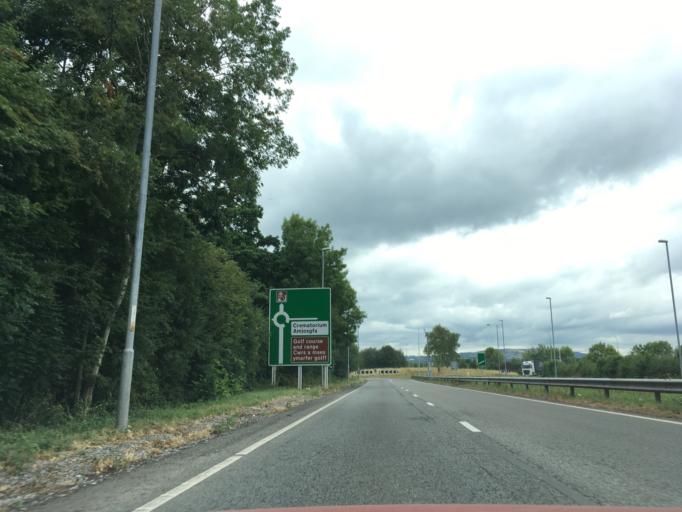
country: GB
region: Wales
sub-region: Torfaen County Borough
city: Cwmbran
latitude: 51.6659
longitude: -3.0041
